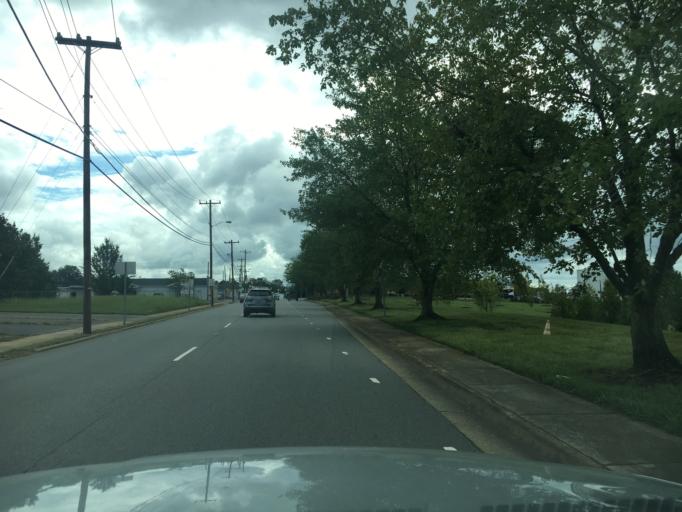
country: US
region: North Carolina
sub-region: Catawba County
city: Hickory
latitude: 35.7391
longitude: -81.3112
